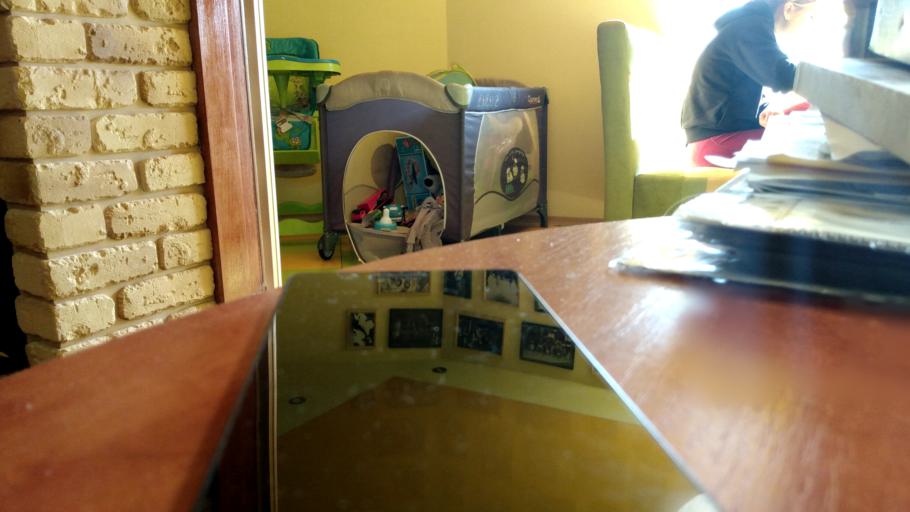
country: RU
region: Penza
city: Serdobsk
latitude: 52.3944
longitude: 44.3316
